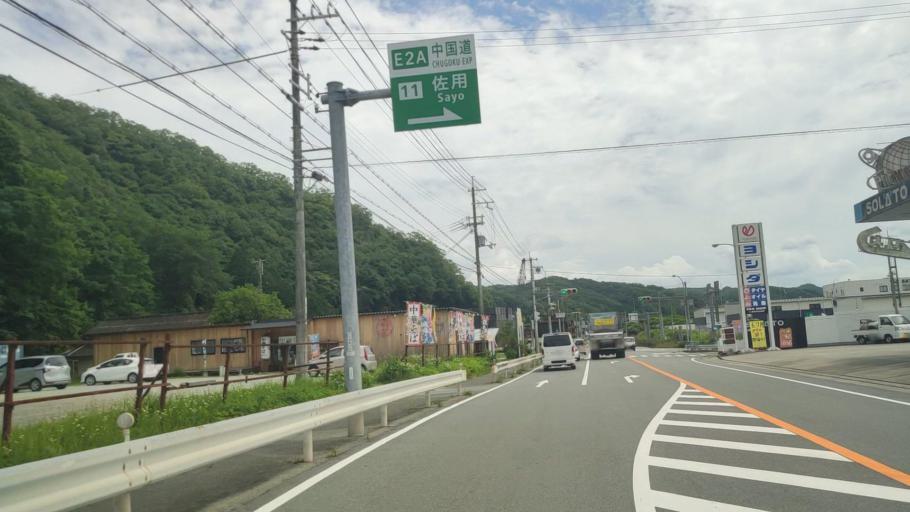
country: JP
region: Hyogo
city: Yamazakicho-nakabirose
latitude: 35.0250
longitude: 134.3712
